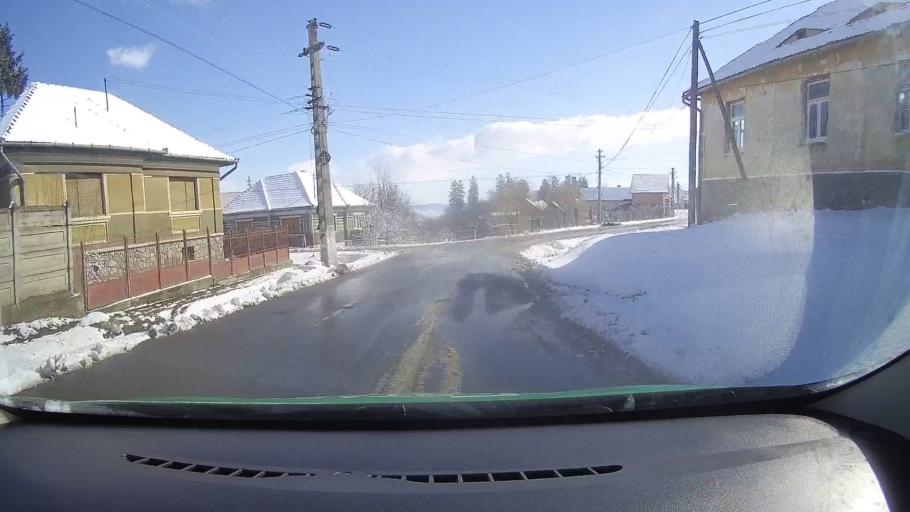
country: RO
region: Sibiu
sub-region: Comuna Rosia
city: Rosia
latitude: 45.8170
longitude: 24.3107
